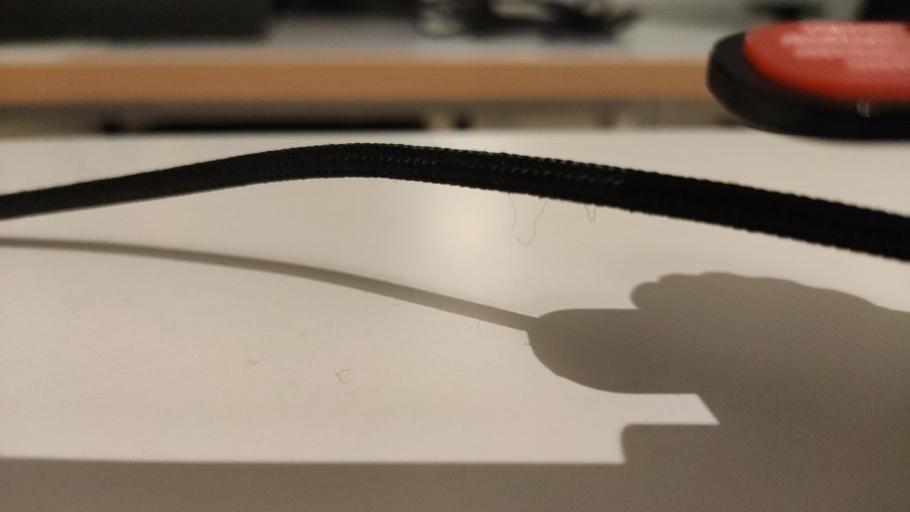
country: RU
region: Moskovskaya
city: Gorshkovo
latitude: 56.3740
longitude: 37.4125
